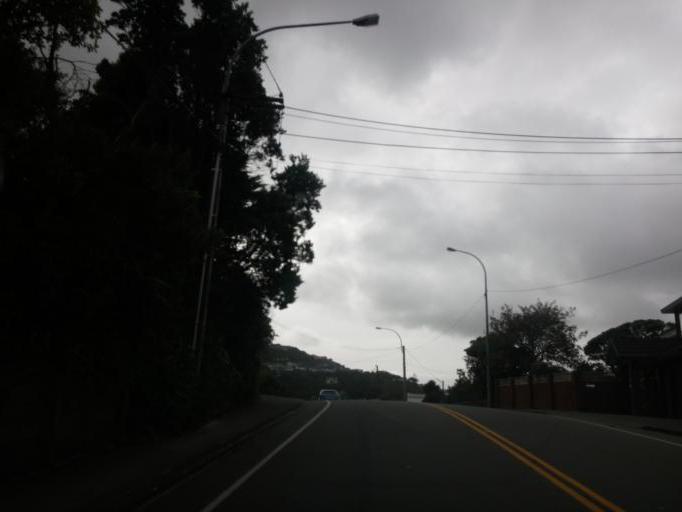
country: NZ
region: Wellington
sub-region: Wellington City
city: Wellington
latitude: -41.2442
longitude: 174.7911
